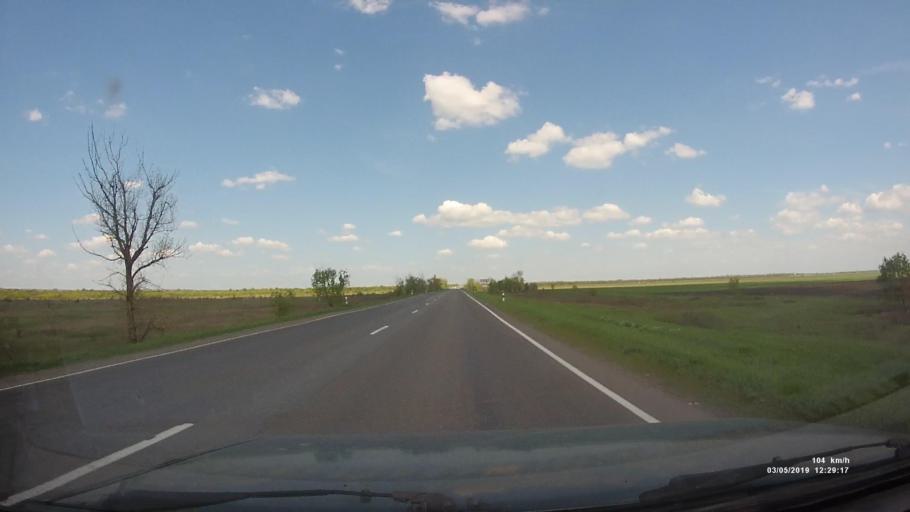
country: RU
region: Rostov
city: Semikarakorsk
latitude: 47.4855
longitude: 40.7358
